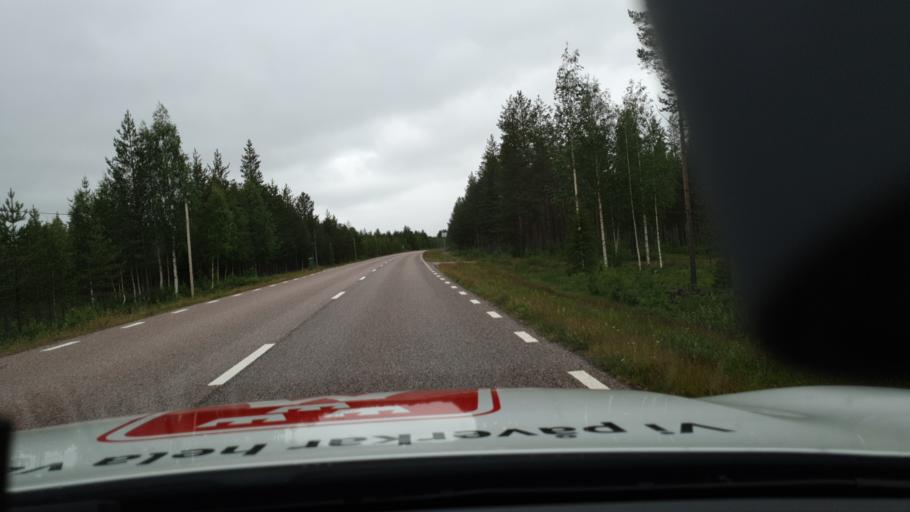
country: FI
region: Lapland
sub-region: Tunturi-Lappi
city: Kolari
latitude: 67.0389
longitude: 23.6993
